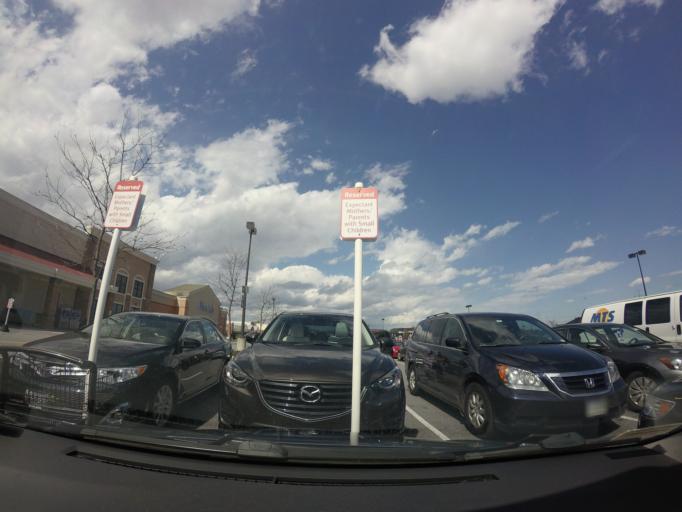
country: US
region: Maryland
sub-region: Frederick County
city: Clover Hill
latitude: 39.4460
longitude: -77.3992
